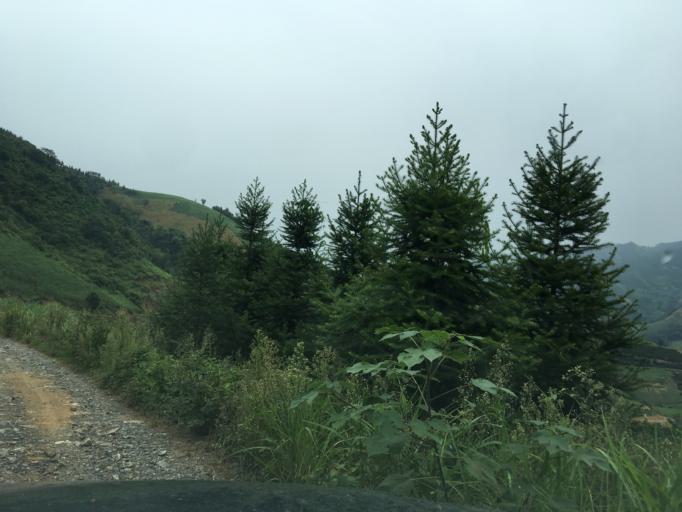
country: CN
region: Guangxi Zhuangzu Zizhiqu
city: Tongle
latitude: 25.0037
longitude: 105.9866
